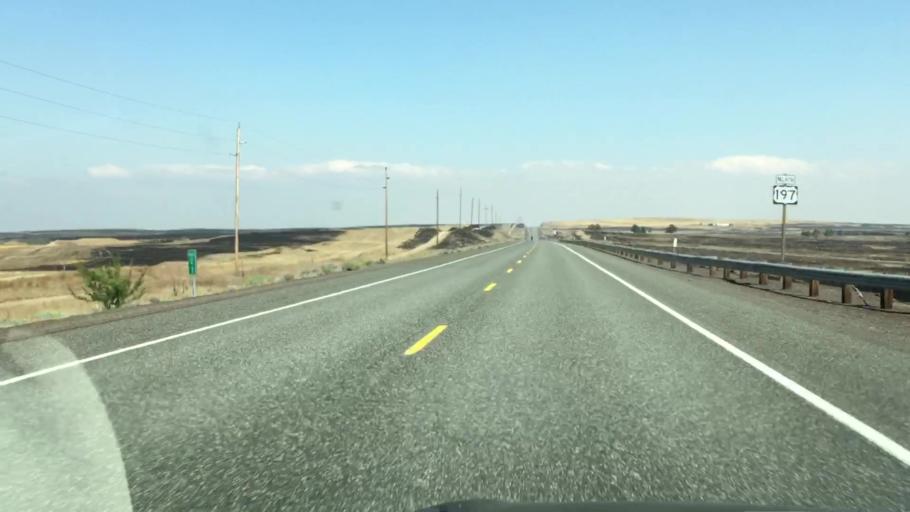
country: US
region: Oregon
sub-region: Wasco County
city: The Dalles
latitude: 45.3446
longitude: -121.1421
